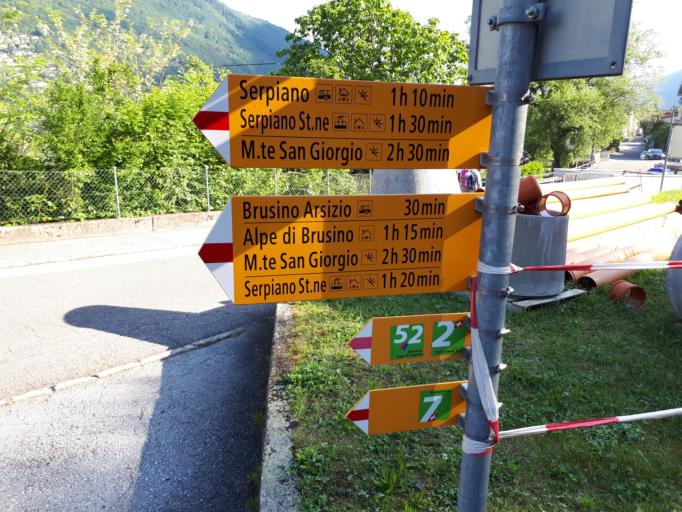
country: CH
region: Ticino
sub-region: Lugano District
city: Melide
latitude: 45.9240
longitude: 8.9345
